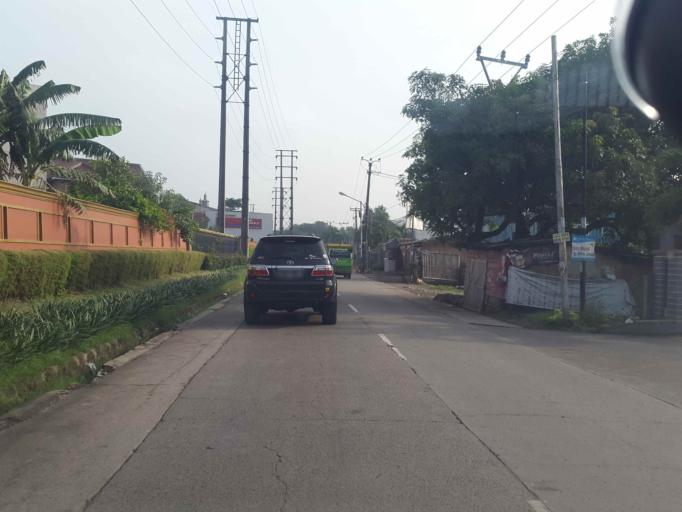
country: ID
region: West Java
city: Bekasi
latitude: -6.2794
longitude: 107.0398
